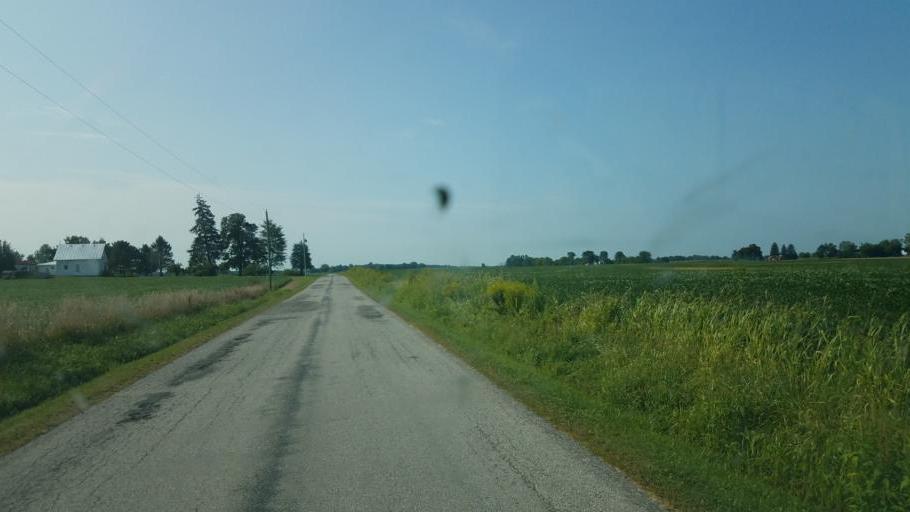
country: US
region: Ohio
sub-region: Morrow County
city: Cardington
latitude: 40.5645
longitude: -82.9193
